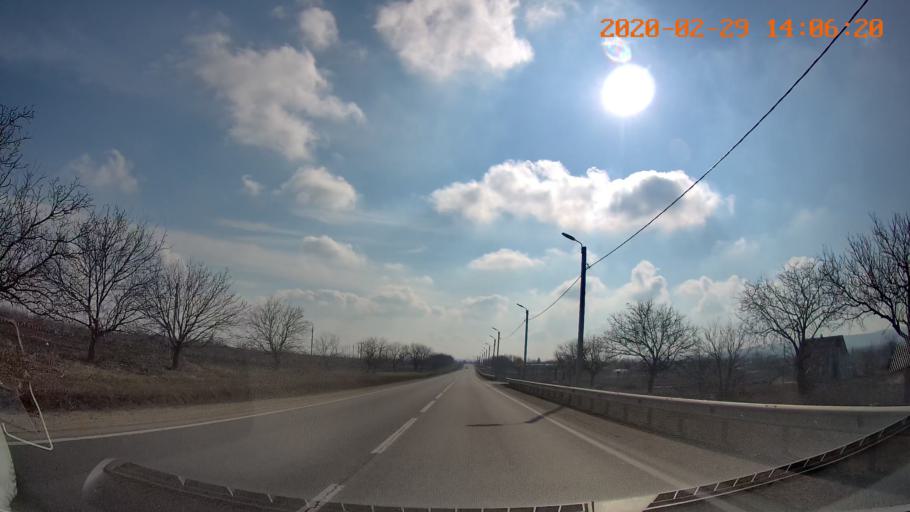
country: MD
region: Taraclia
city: Telenesti
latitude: 47.6667
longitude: 28.4915
